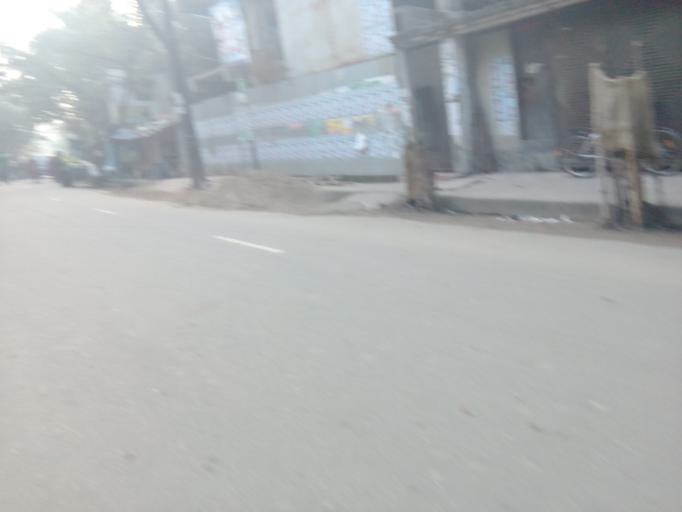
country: BD
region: Dhaka
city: Paltan
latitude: 23.7511
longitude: 90.4179
